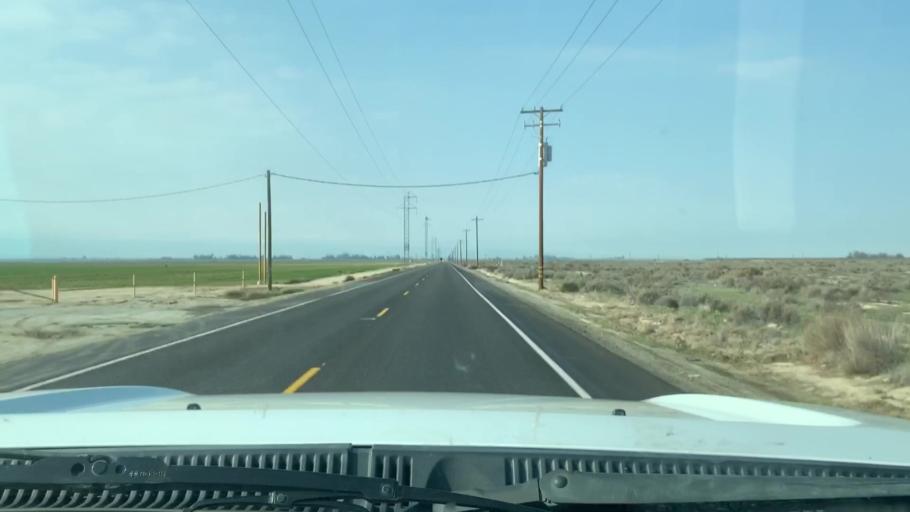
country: US
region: California
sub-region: Kern County
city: Shafter
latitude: 35.4421
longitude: -119.3582
